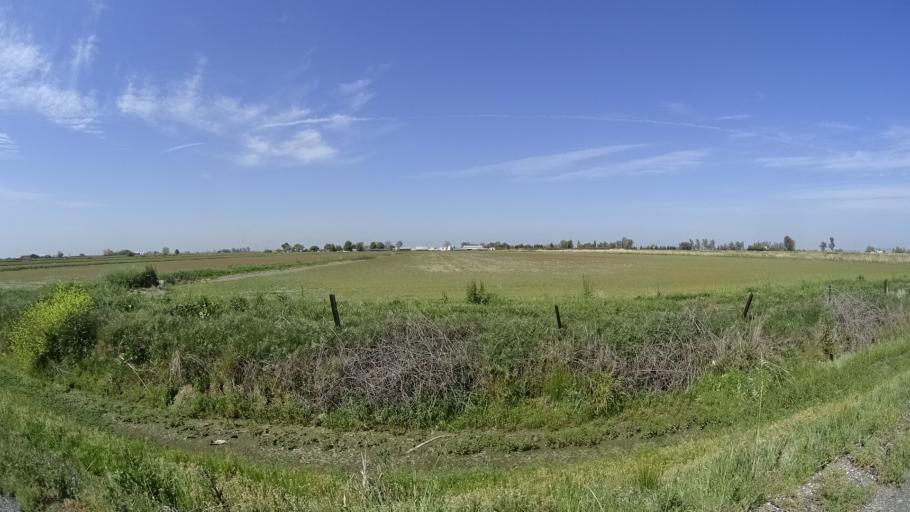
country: US
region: California
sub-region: Glenn County
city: Hamilton City
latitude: 39.5789
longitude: -122.0276
